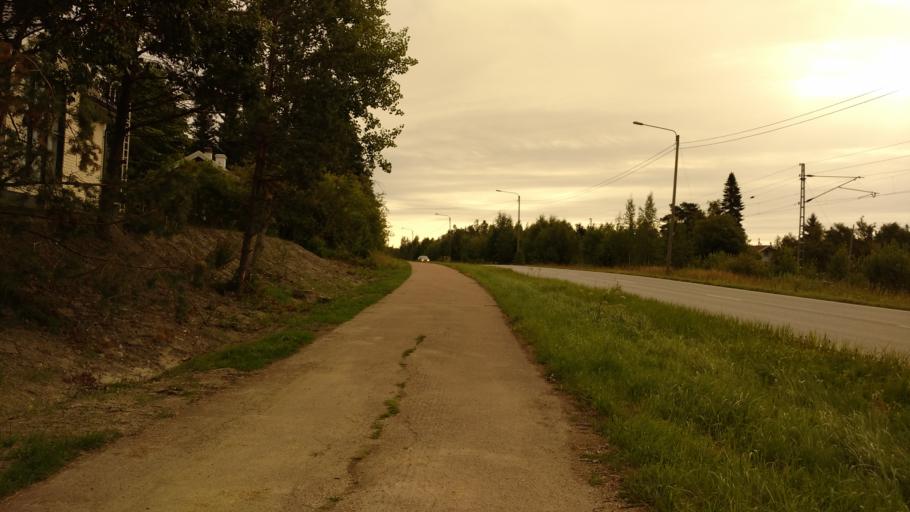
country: FI
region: Varsinais-Suomi
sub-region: Turku
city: Kaarina
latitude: 60.4429
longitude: 22.3866
